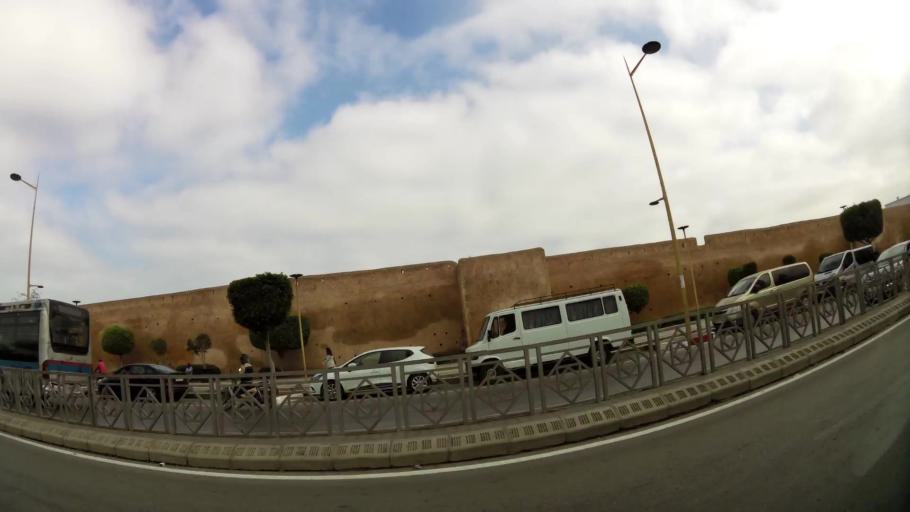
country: MA
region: Rabat-Sale-Zemmour-Zaer
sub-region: Rabat
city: Rabat
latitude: 34.0246
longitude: -6.8321
